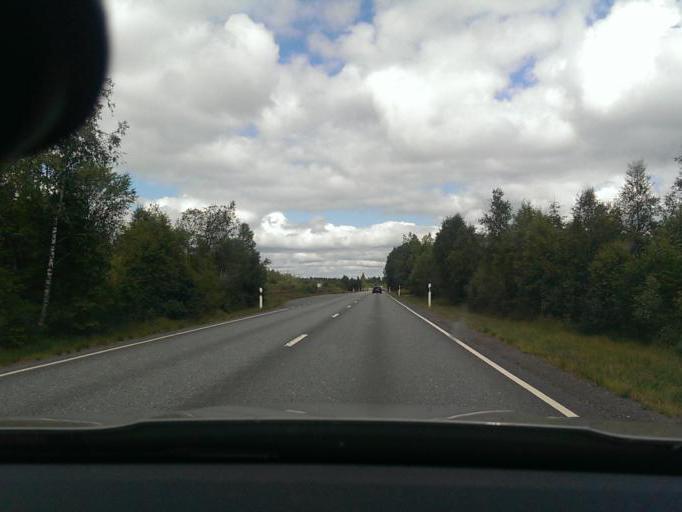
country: SE
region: Joenkoeping
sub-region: Varnamo Kommun
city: Varnamo
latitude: 57.2588
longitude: 13.9812
